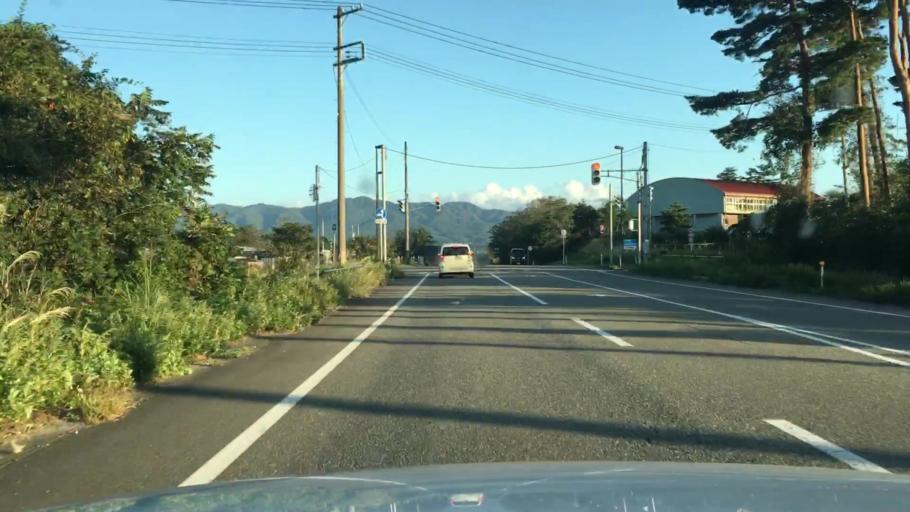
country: JP
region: Niigata
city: Murakami
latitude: 38.1245
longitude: 139.4036
